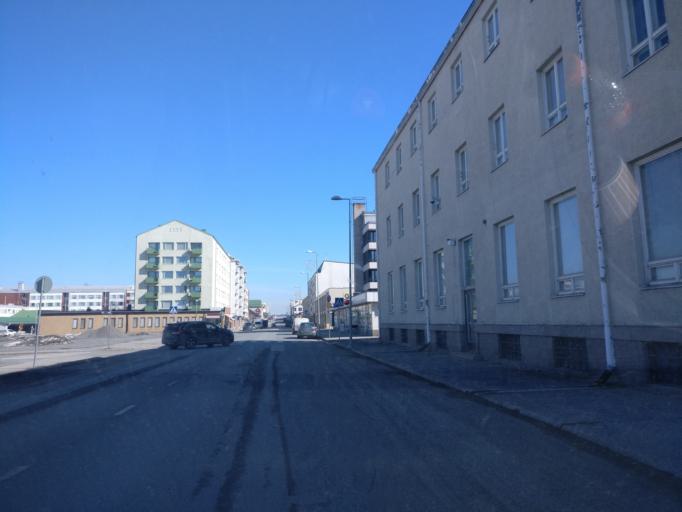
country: FI
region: Lapland
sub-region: Kemi-Tornio
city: Kemi
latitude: 65.7348
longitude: 24.5601
